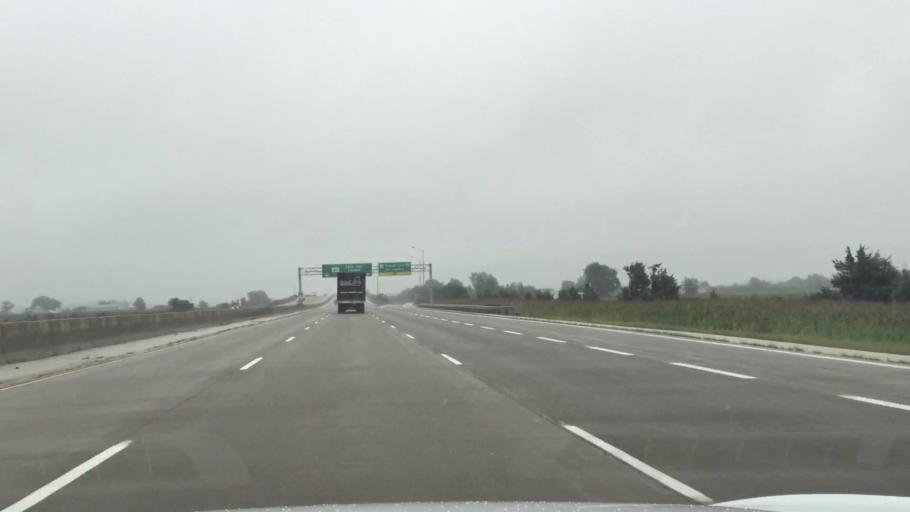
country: US
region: Michigan
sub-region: Wayne County
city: Grosse Pointe Farms
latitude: 42.2334
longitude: -82.6460
